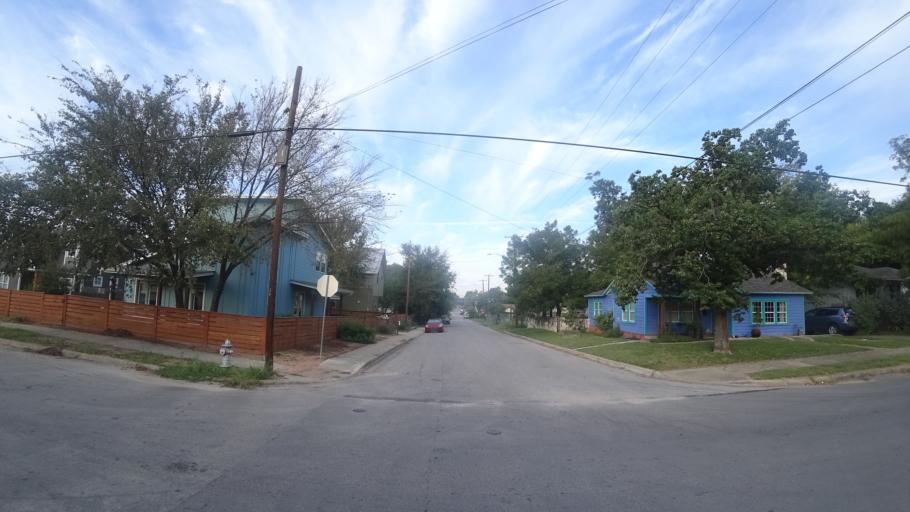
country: US
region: Texas
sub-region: Travis County
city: Austin
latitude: 30.2777
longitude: -97.7137
